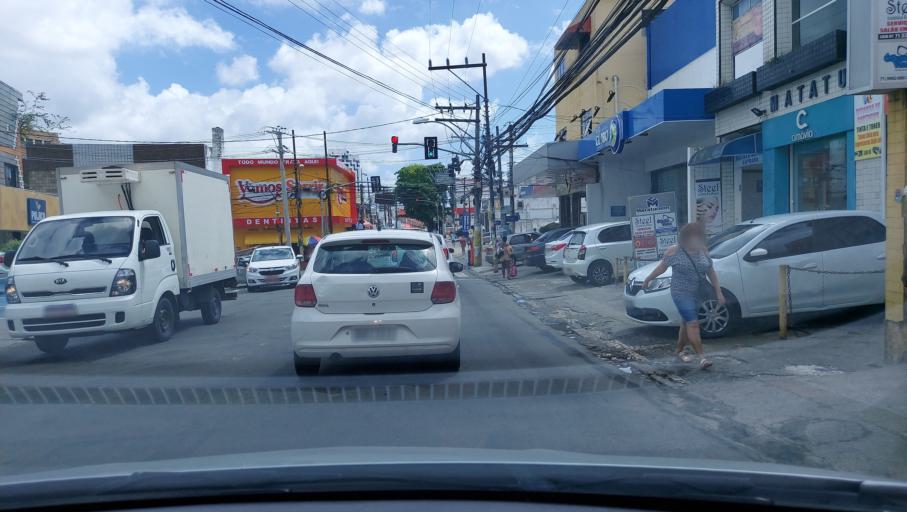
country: BR
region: Bahia
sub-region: Salvador
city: Salvador
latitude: -12.9740
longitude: -38.4932
